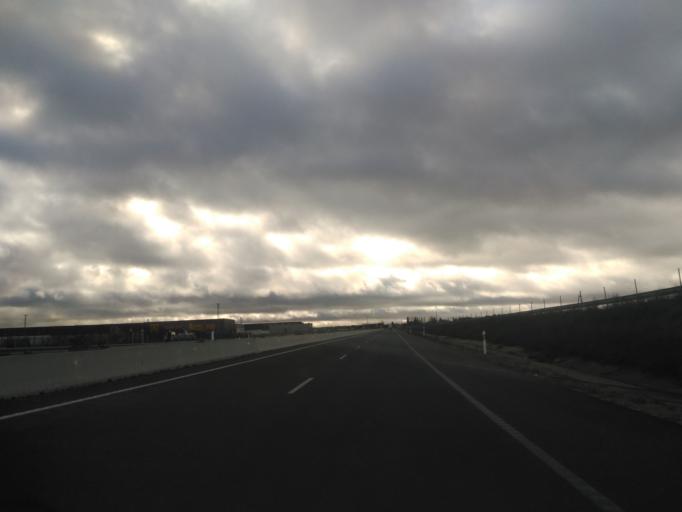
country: ES
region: Castille and Leon
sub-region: Provincia de Zamora
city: Morales del Vino
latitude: 41.4647
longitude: -5.7344
